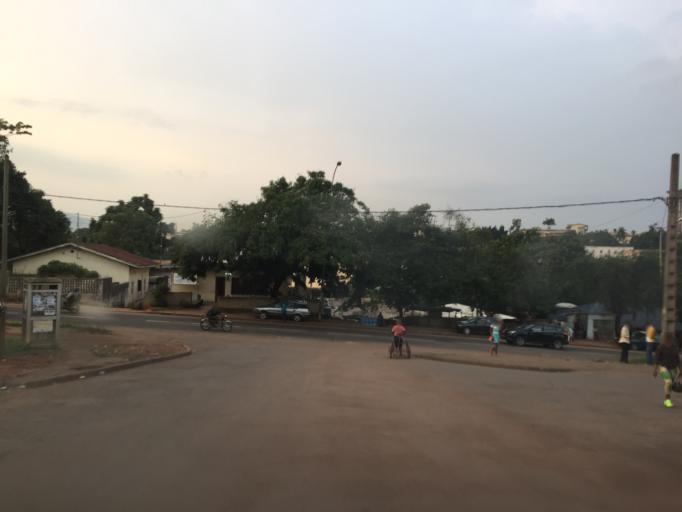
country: CM
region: Centre
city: Yaounde
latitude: 3.8682
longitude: 11.5072
